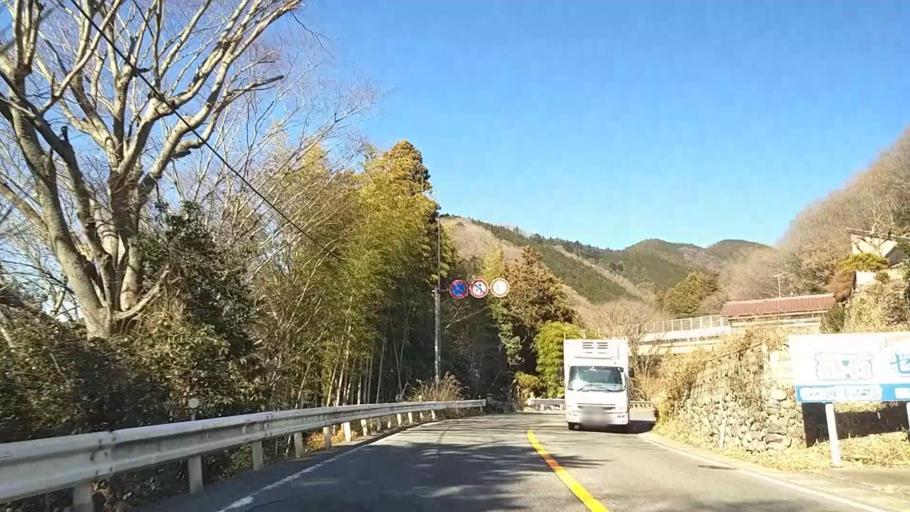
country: JP
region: Yamanashi
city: Uenohara
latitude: 35.6191
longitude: 139.1813
